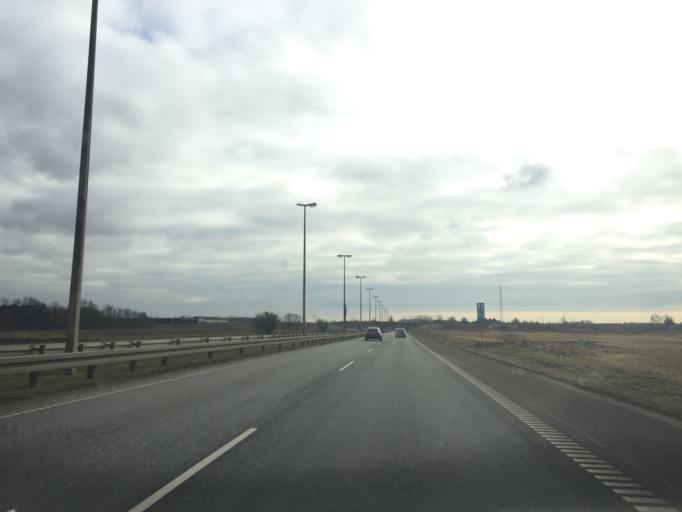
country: DK
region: Capital Region
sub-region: Hoje-Taastrup Kommune
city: Taastrup
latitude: 55.6256
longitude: 12.3127
